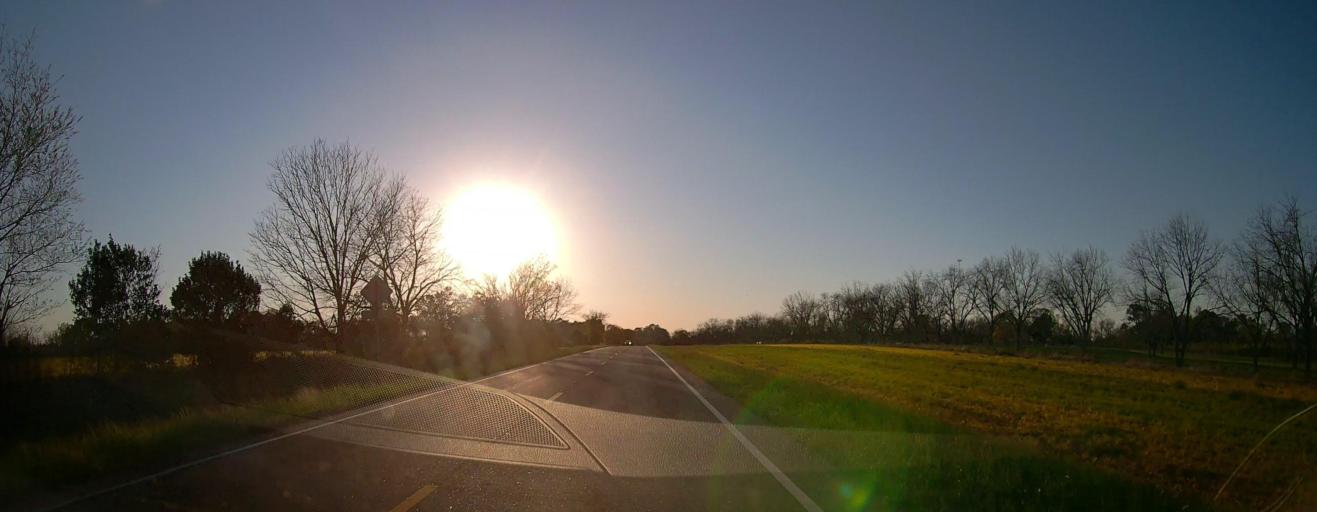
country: US
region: Georgia
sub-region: Wilcox County
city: Rochelle
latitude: 31.9454
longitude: -83.5247
